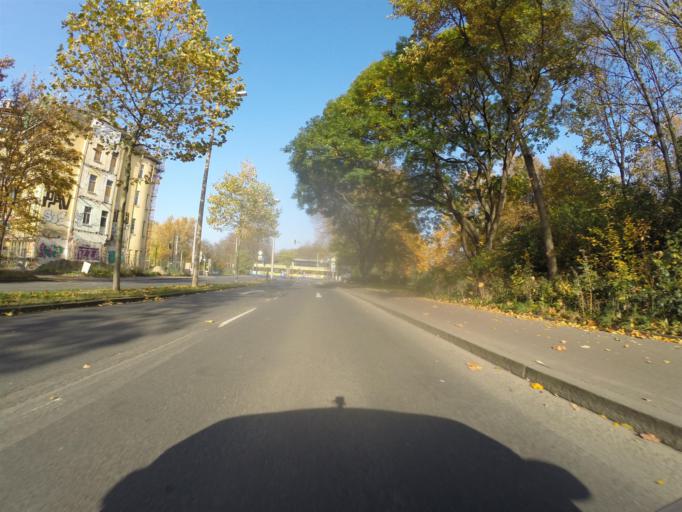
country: DE
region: Saxony
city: Leipzig
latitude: 51.3379
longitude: 12.3427
